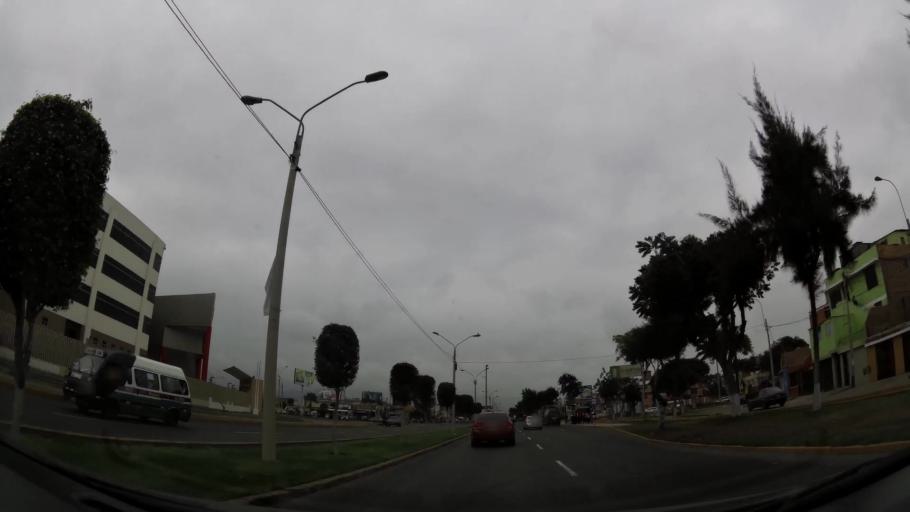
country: PE
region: Callao
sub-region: Callao
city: Callao
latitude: -12.0572
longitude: -77.1157
